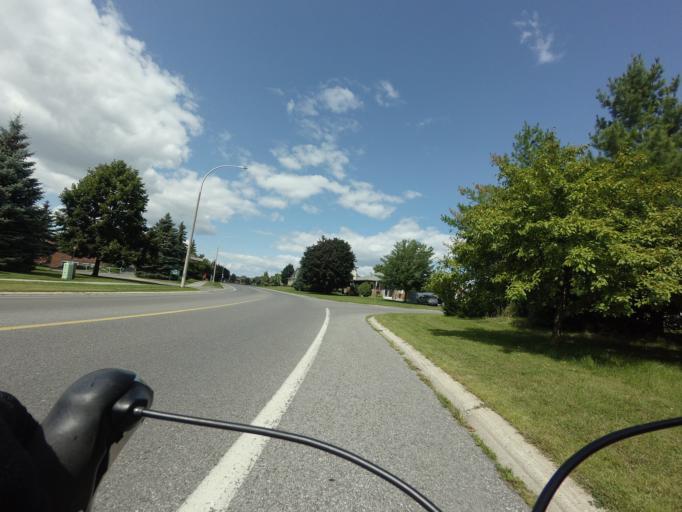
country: CA
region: Ontario
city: Bells Corners
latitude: 45.2926
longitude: -75.8492
